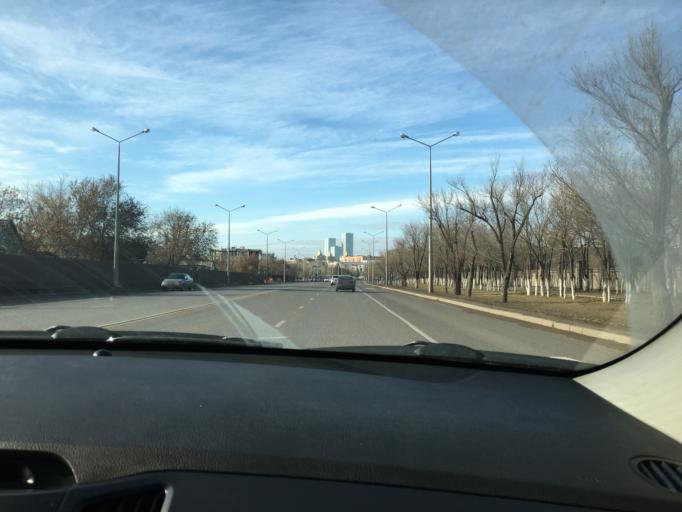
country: KZ
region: Astana Qalasy
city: Astana
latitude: 51.1575
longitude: 71.4479
